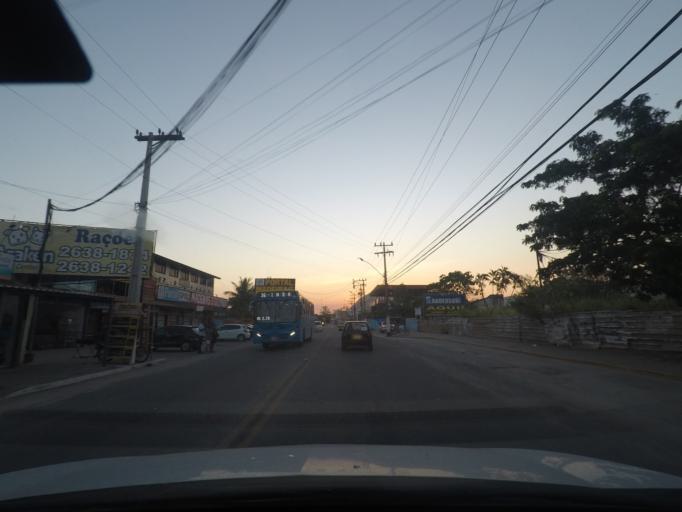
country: BR
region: Rio de Janeiro
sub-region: Niteroi
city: Niteroi
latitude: -22.9581
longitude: -42.9813
